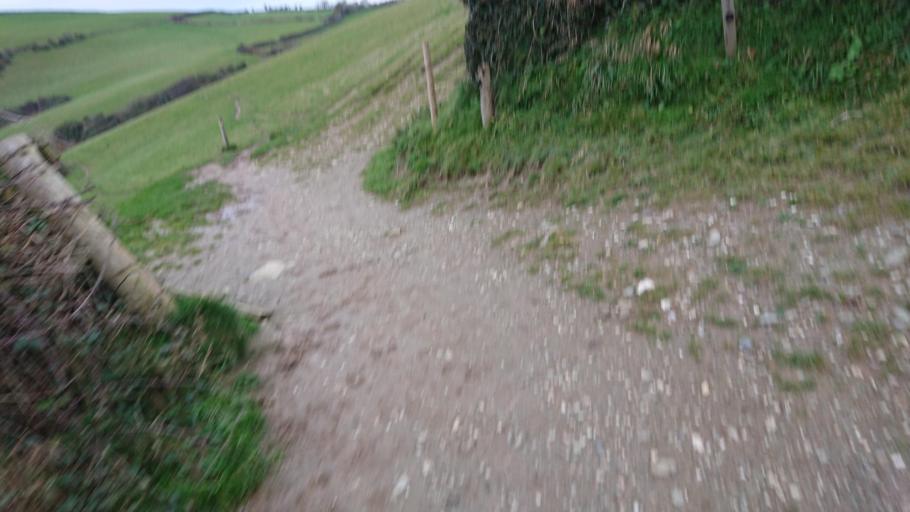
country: GB
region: England
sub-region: Cornwall
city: Fowey
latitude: 50.3324
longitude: -4.5825
